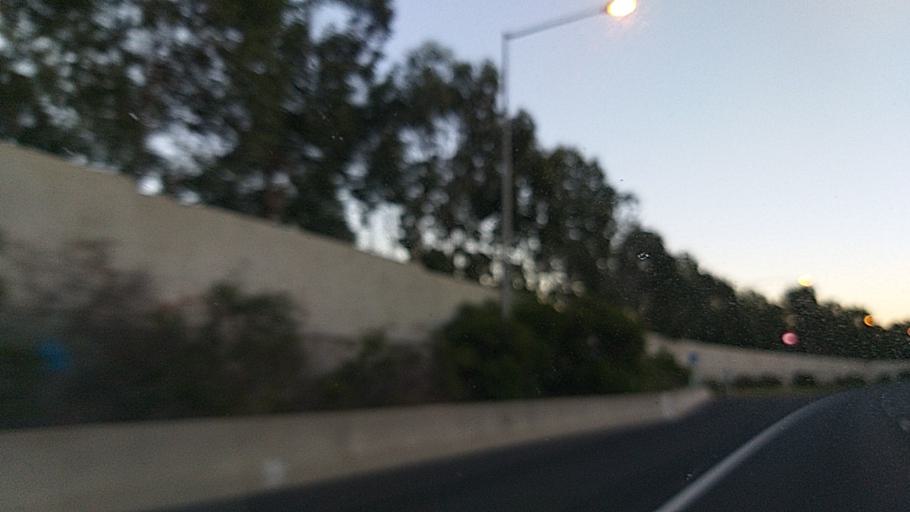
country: AU
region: New South Wales
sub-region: Blacktown
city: Doonside
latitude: -33.7690
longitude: 150.8467
